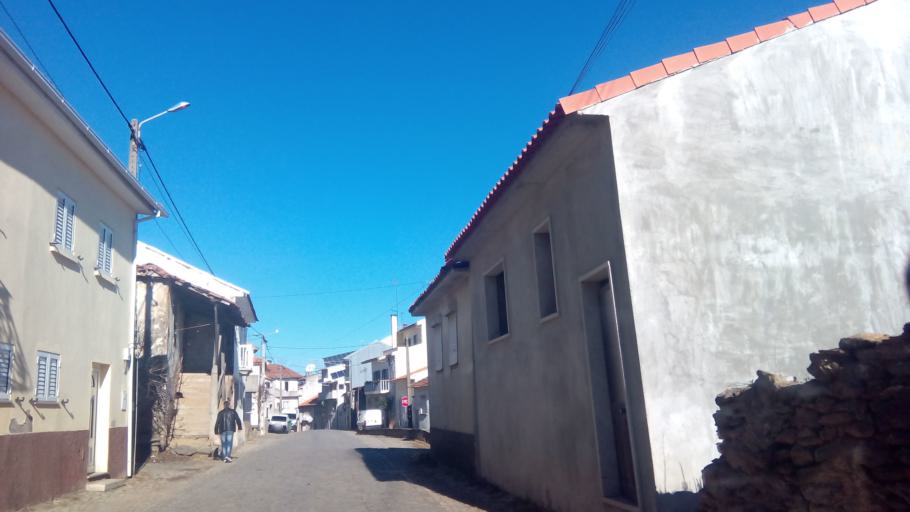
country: PT
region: Braganca
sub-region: Vimioso
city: Vimioso
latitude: 41.6402
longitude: -6.6012
